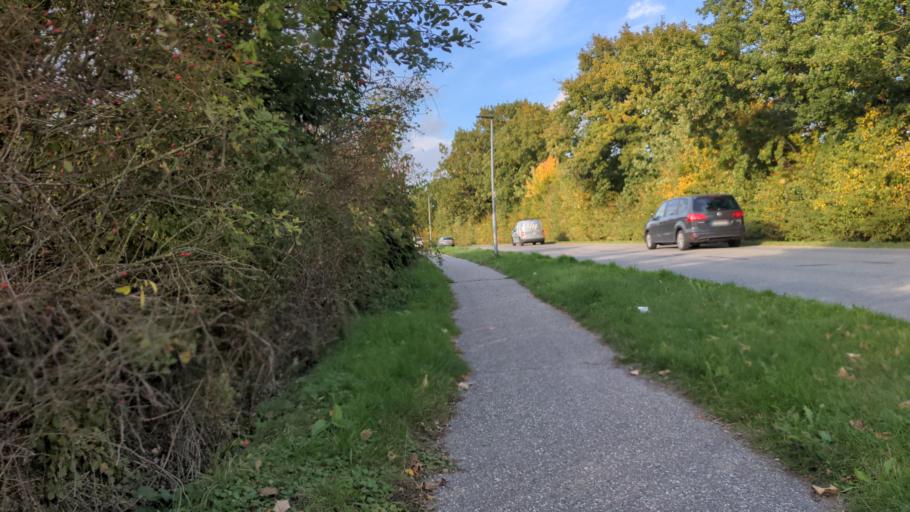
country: DE
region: Schleswig-Holstein
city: Ahrensbok
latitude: 54.0085
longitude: 10.5822
